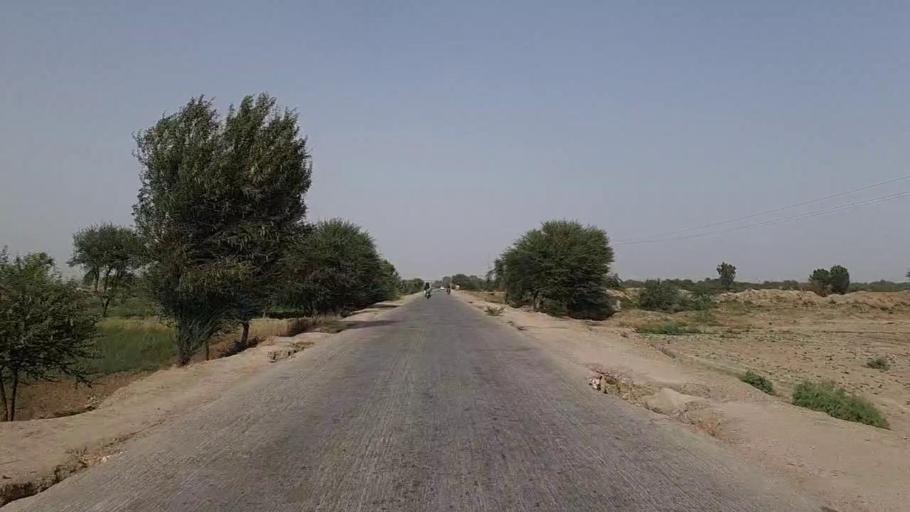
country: PK
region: Sindh
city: Tando Bago
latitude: 24.9173
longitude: 69.1002
